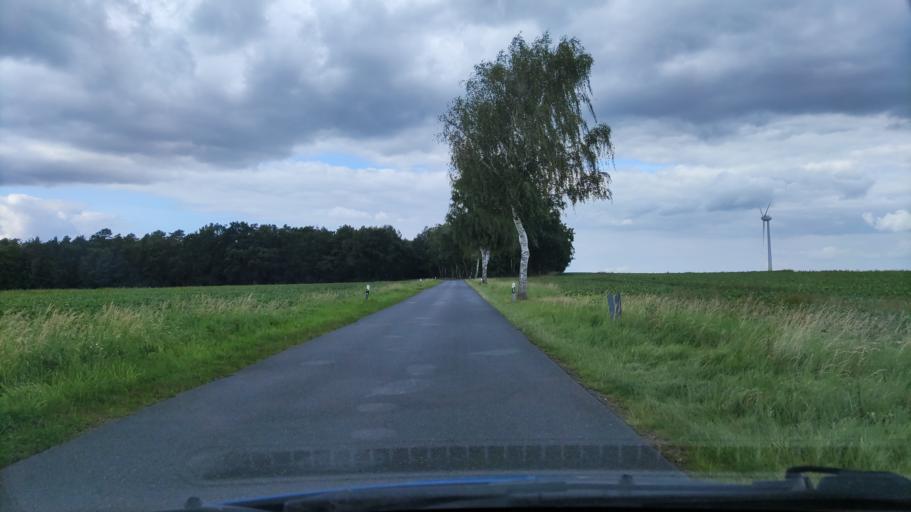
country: DE
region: Lower Saxony
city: Weste
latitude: 53.0493
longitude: 10.7160
